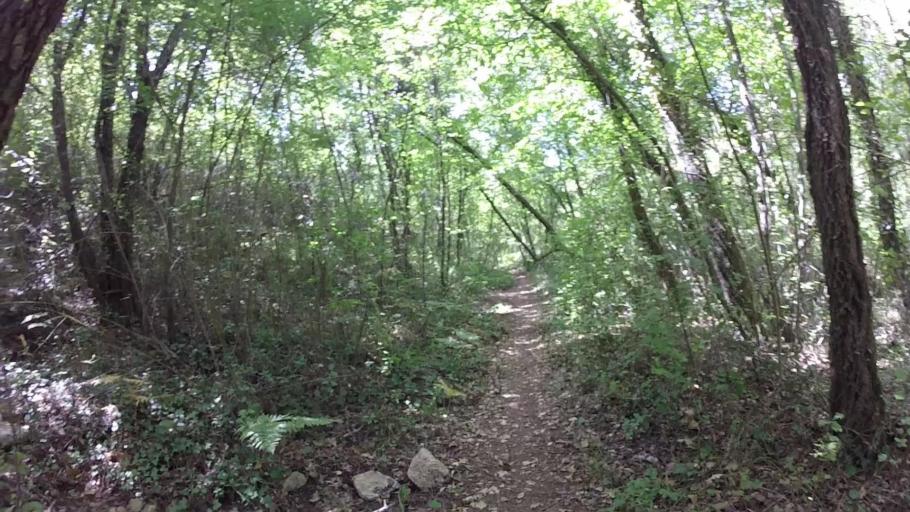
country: FR
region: Provence-Alpes-Cote d'Azur
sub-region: Departement des Alpes-Maritimes
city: Mougins
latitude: 43.6170
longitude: 7.0275
